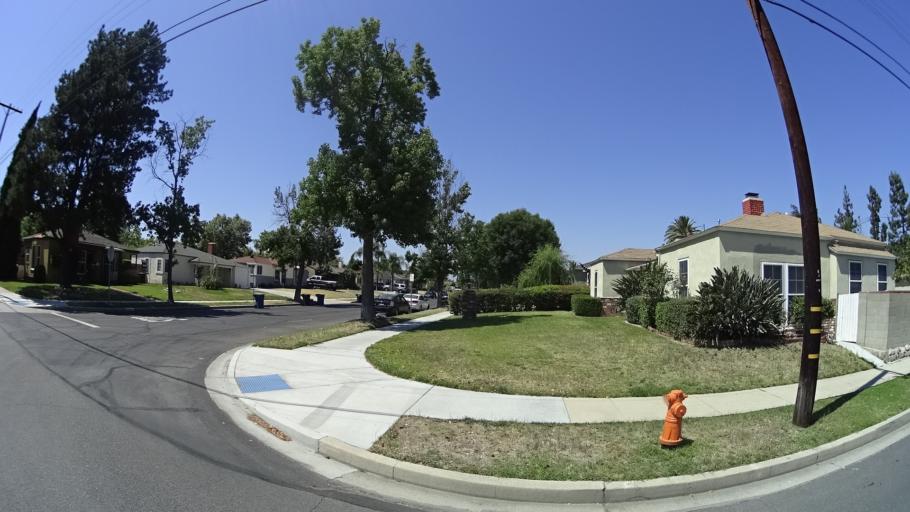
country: US
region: California
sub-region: Los Angeles County
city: North Hollywood
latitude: 34.1811
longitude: -118.3555
